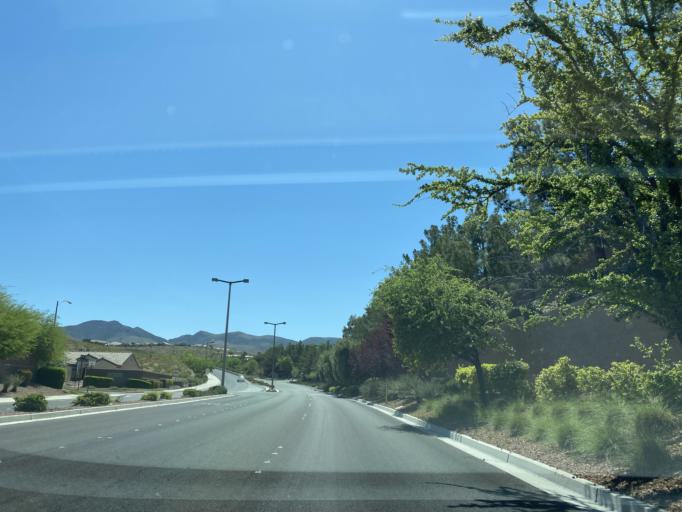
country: US
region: Nevada
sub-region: Clark County
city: Whitney
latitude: 35.9414
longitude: -115.1134
